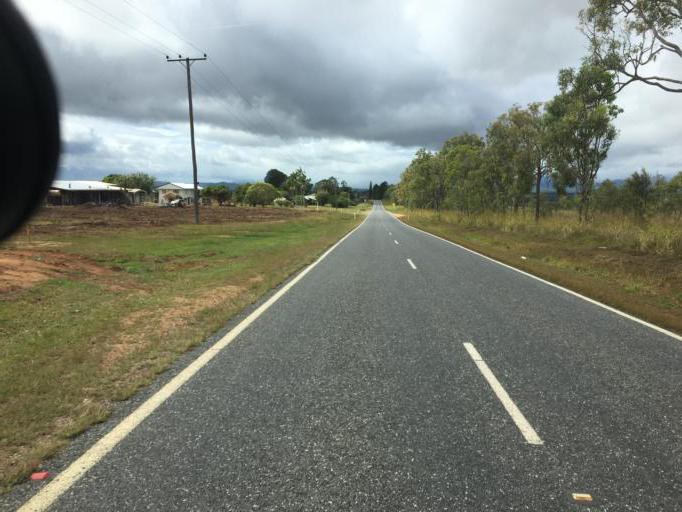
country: AU
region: Queensland
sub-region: Tablelands
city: Mareeba
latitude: -17.0160
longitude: 145.3564
